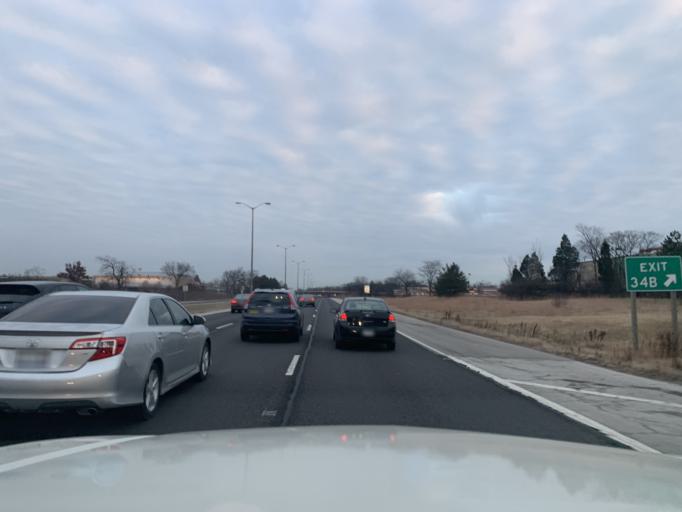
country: US
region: Illinois
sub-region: Cook County
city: Northfield
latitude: 42.0804
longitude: -87.7585
